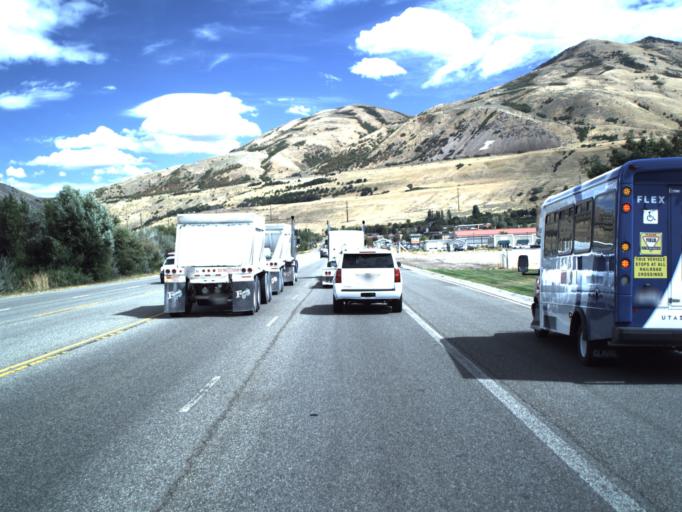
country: US
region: Utah
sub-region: Box Elder County
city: Perry
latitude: 41.4865
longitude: -112.0277
